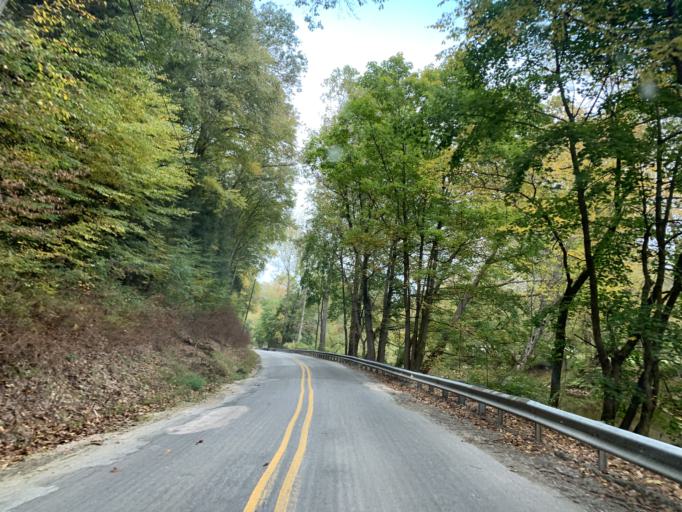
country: US
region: Pennsylvania
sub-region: York County
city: Susquehanna Trails
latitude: 39.7894
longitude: -76.4182
